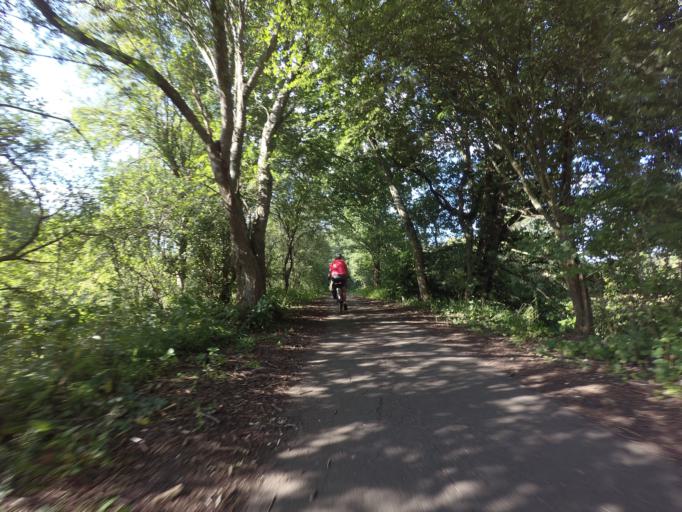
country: GB
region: England
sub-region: East Sussex
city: Horam
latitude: 50.9041
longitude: 0.2603
